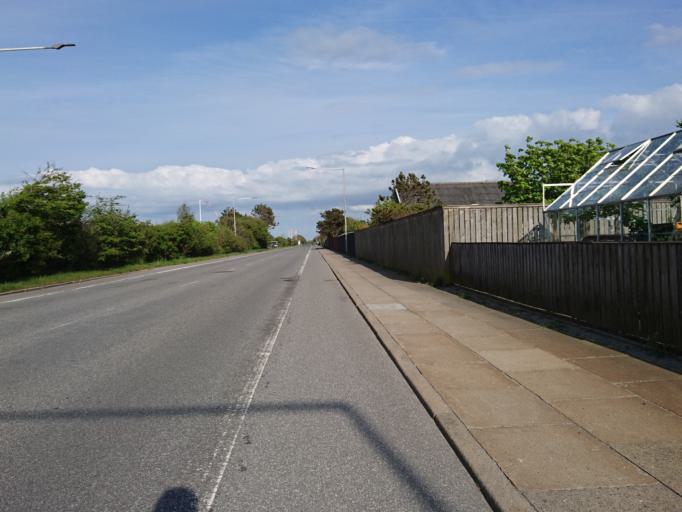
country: DK
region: North Denmark
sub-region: Frederikshavn Kommune
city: Skagen
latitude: 57.7294
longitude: 10.5433
